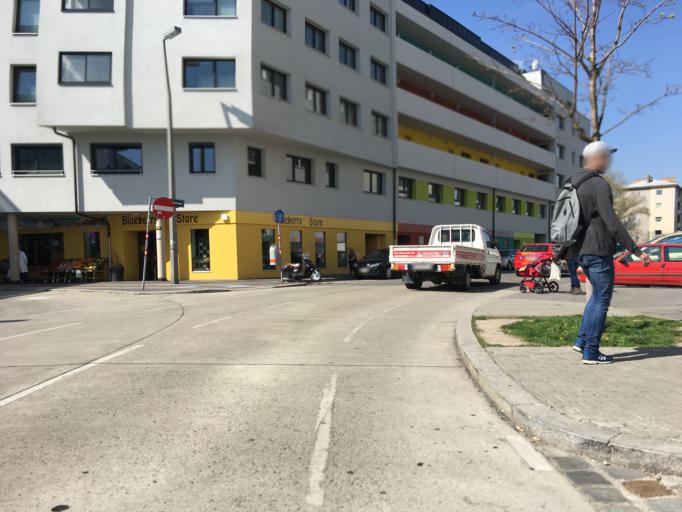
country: AT
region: Lower Austria
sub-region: Politischer Bezirk Wien-Umgebung
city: Gerasdorf bei Wien
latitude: 48.2212
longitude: 16.4576
